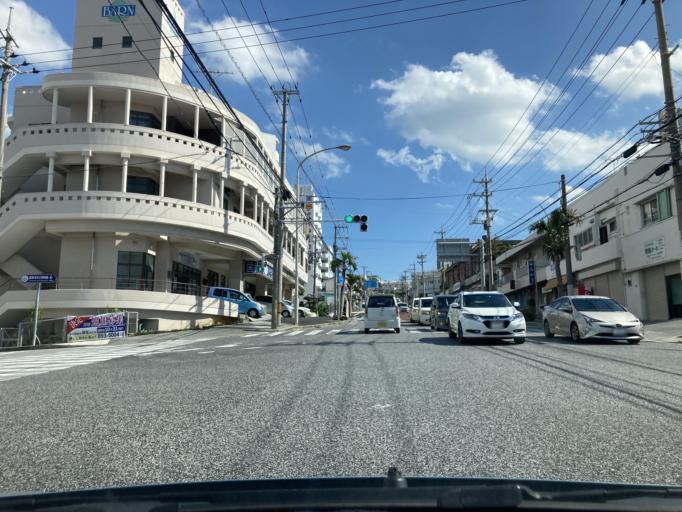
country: JP
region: Okinawa
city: Ginowan
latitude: 26.2670
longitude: 127.7359
